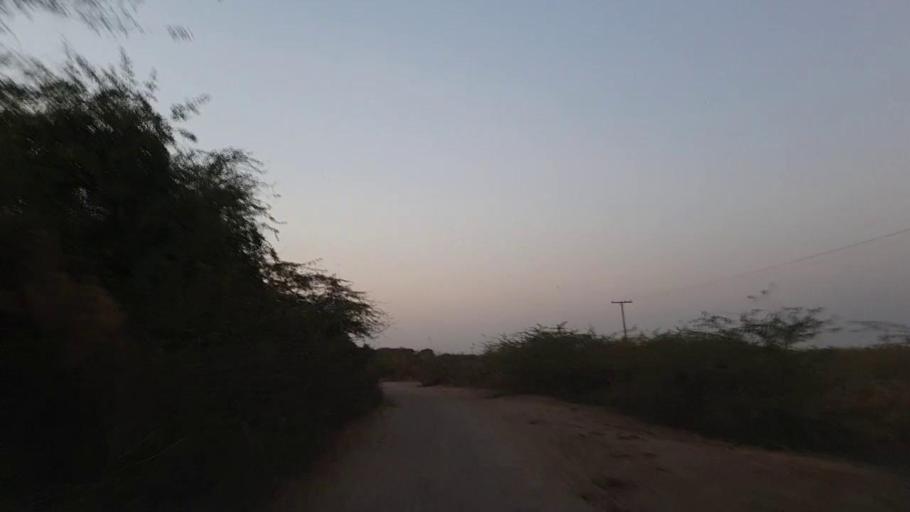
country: PK
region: Sindh
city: Naukot
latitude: 24.8893
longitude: 69.3849
